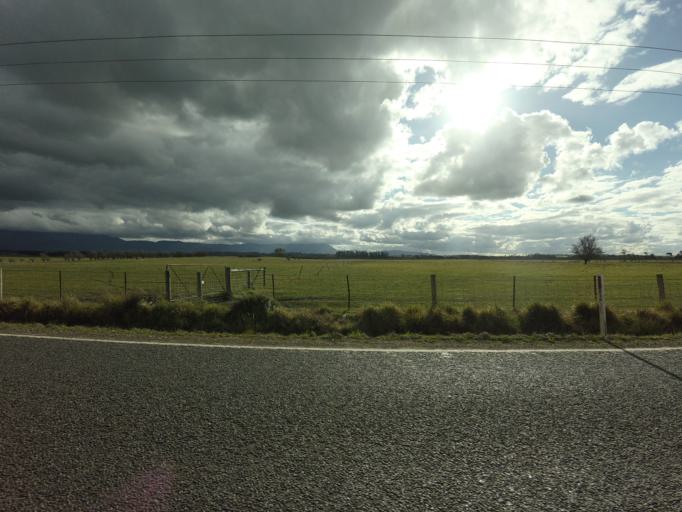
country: AU
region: Tasmania
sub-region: Northern Midlands
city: Longford
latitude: -41.7403
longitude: 147.0827
